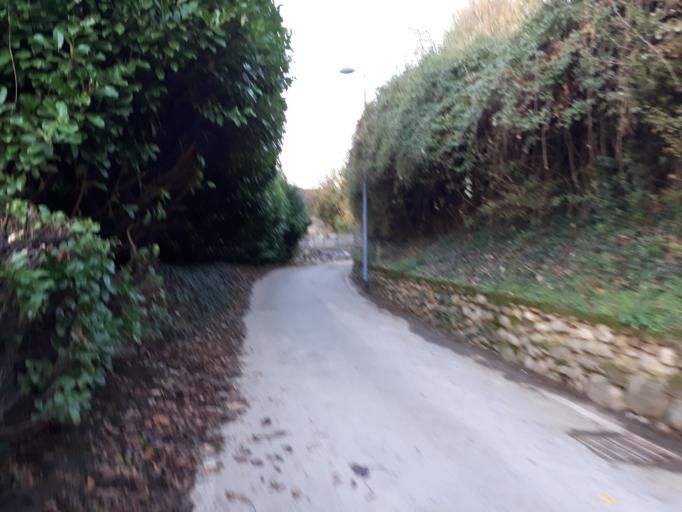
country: IT
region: Lombardy
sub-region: Provincia di Lecco
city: Cernusco Lombardone
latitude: 45.6935
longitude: 9.3938
